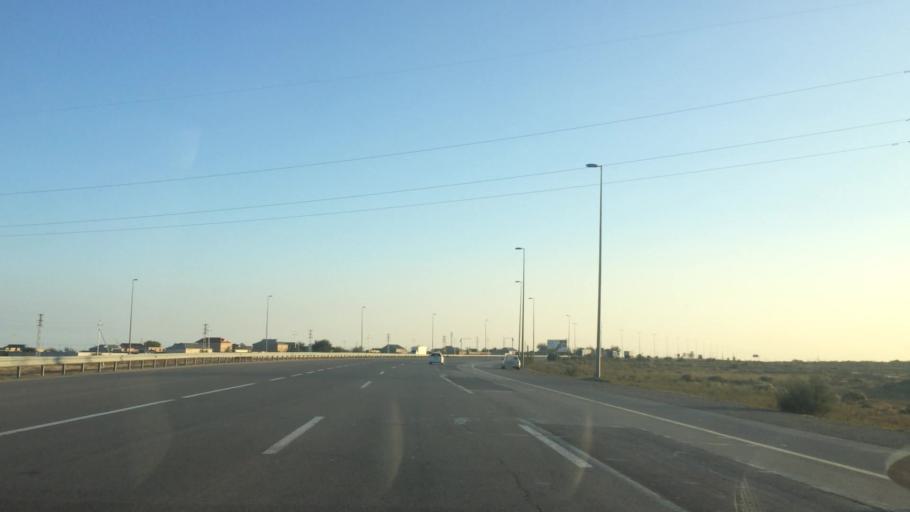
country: AZ
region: Baki
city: Qobustan
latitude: 39.9929
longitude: 49.4306
